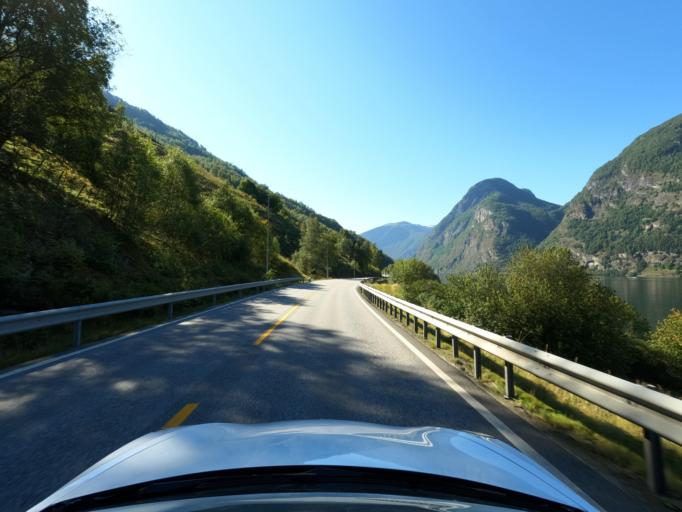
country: NO
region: Sogn og Fjordane
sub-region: Aurland
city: Aurlandsvangen
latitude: 60.8951
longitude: 7.1667
